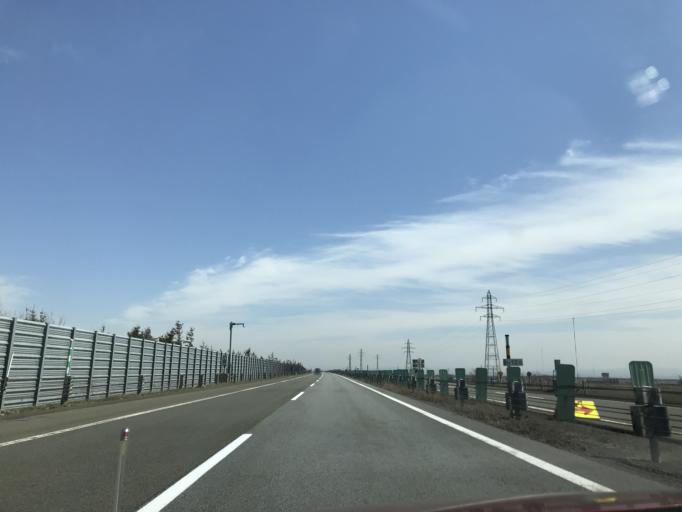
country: JP
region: Hokkaido
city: Ebetsu
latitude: 43.0865
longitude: 141.5634
